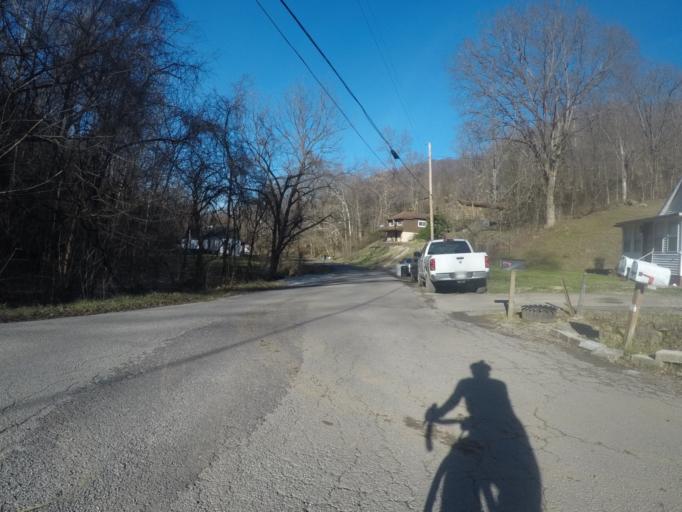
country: US
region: West Virginia
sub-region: Cabell County
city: Huntington
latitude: 38.3922
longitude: -82.4858
